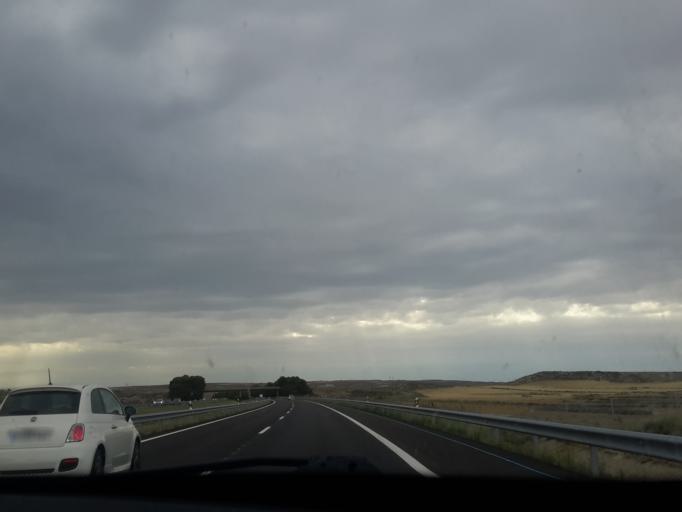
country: ES
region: Aragon
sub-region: Provincia de Huesca
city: Castejon de Monegros
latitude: 41.5277
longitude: -0.3387
